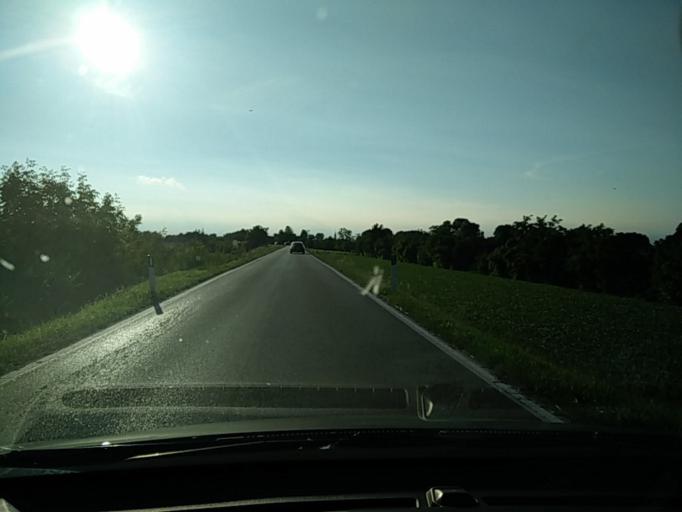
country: IT
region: Veneto
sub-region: Provincia di Venezia
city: San Dona di Piave
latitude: 45.6117
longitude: 12.5818
